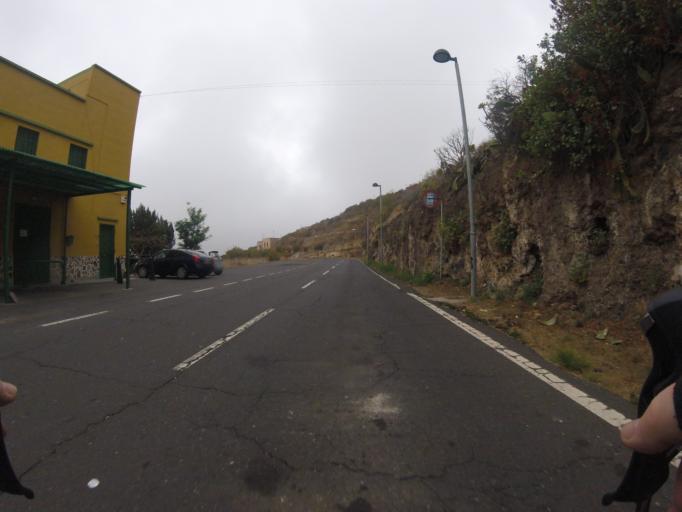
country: ES
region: Canary Islands
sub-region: Provincia de Santa Cruz de Tenerife
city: Guimar
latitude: 28.2834
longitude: -16.4075
